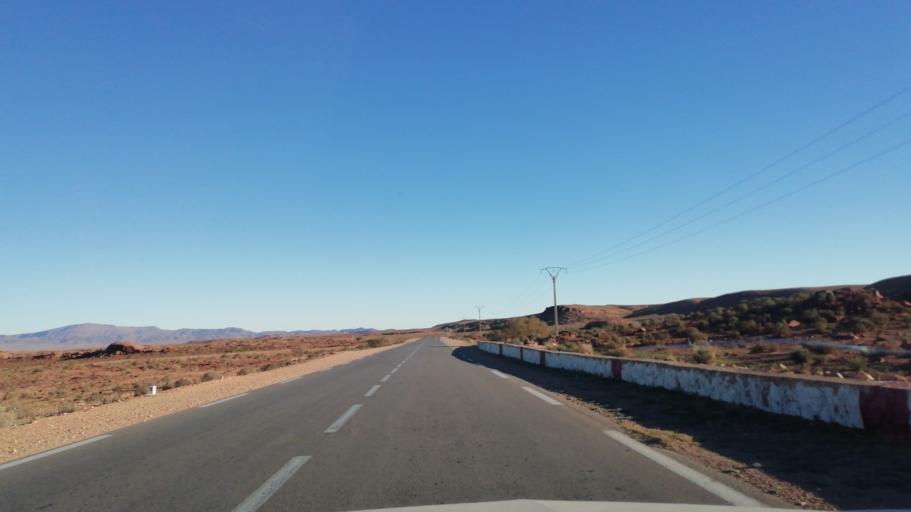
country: DZ
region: El Bayadh
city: El Abiodh Sidi Cheikh
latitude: 33.1705
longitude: 0.4581
